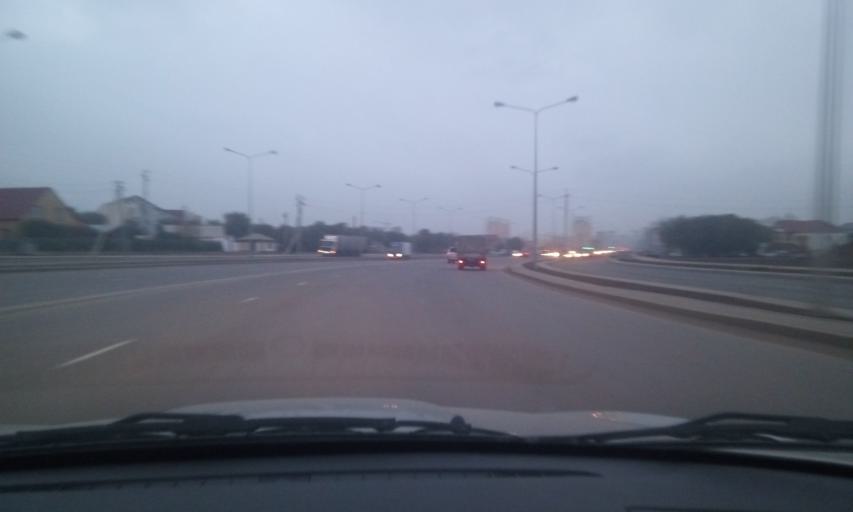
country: KZ
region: Astana Qalasy
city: Astana
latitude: 51.1358
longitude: 71.5200
